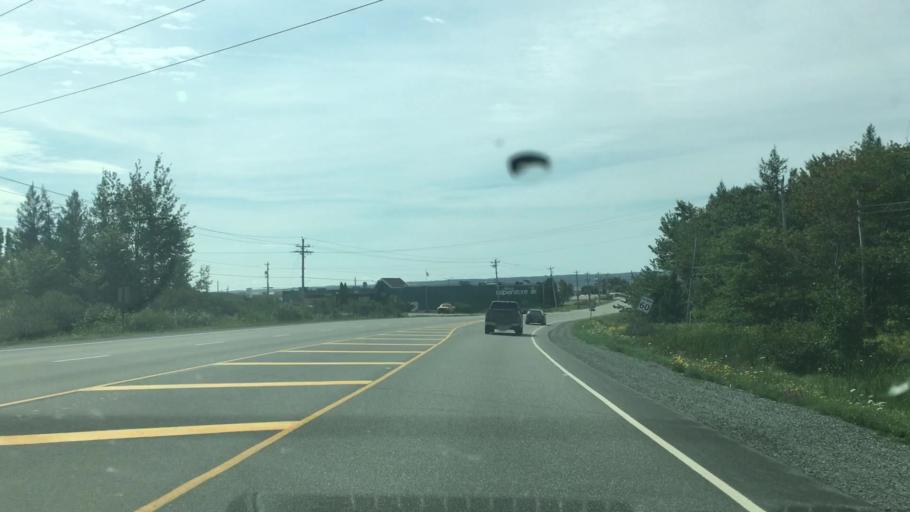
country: CA
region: Nova Scotia
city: Port Hawkesbury
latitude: 45.6219
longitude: -61.3335
